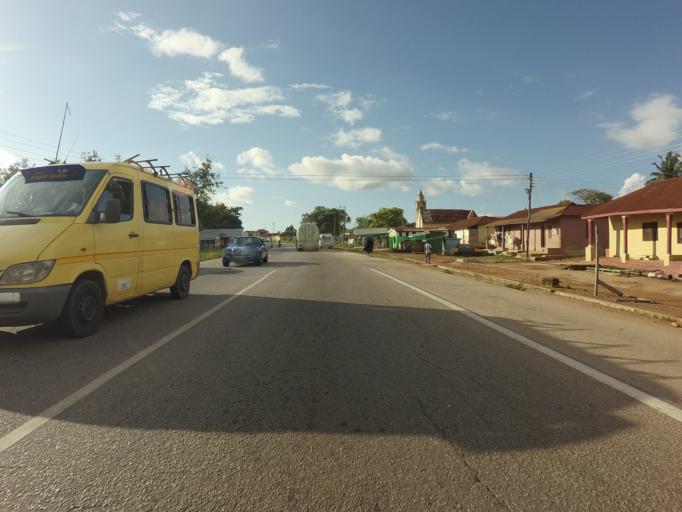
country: GH
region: Ashanti
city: Tafo
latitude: 6.9078
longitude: -1.6556
